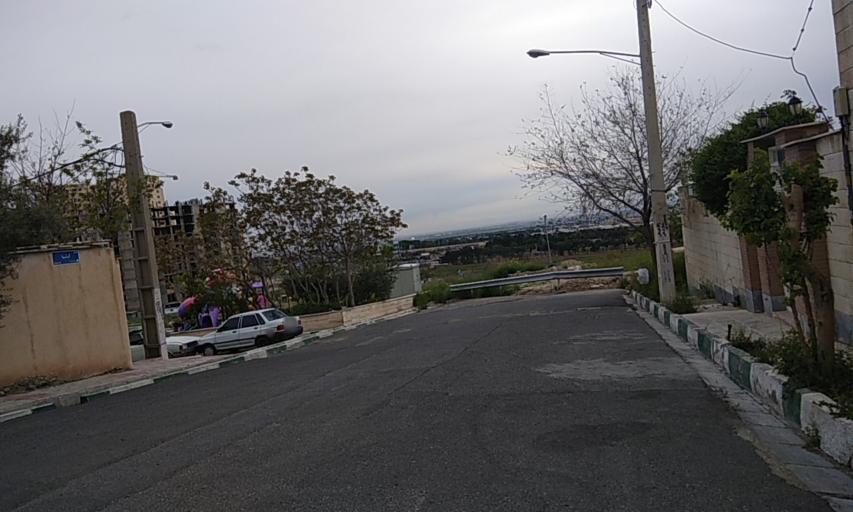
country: IR
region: Tehran
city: Shahr-e Qods
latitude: 35.7531
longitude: 51.1499
